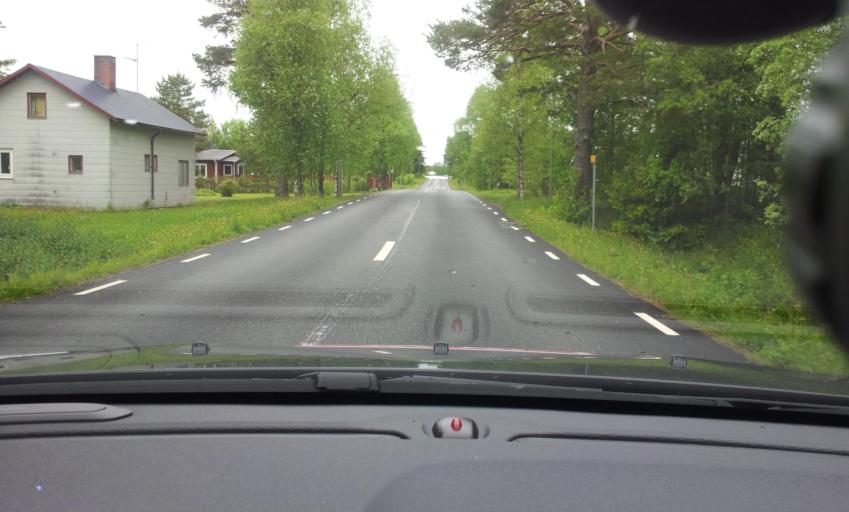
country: SE
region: Jaemtland
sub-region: Krokoms Kommun
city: Valla
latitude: 63.3273
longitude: 14.0310
